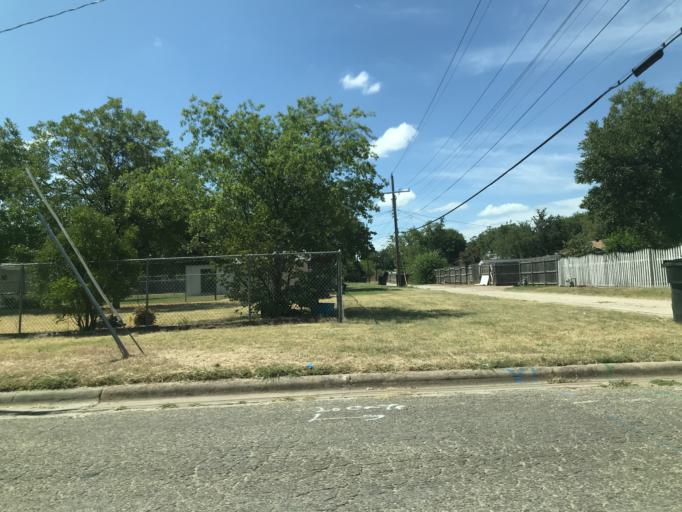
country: US
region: Texas
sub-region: Taylor County
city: Abilene
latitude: 32.4211
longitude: -99.7578
